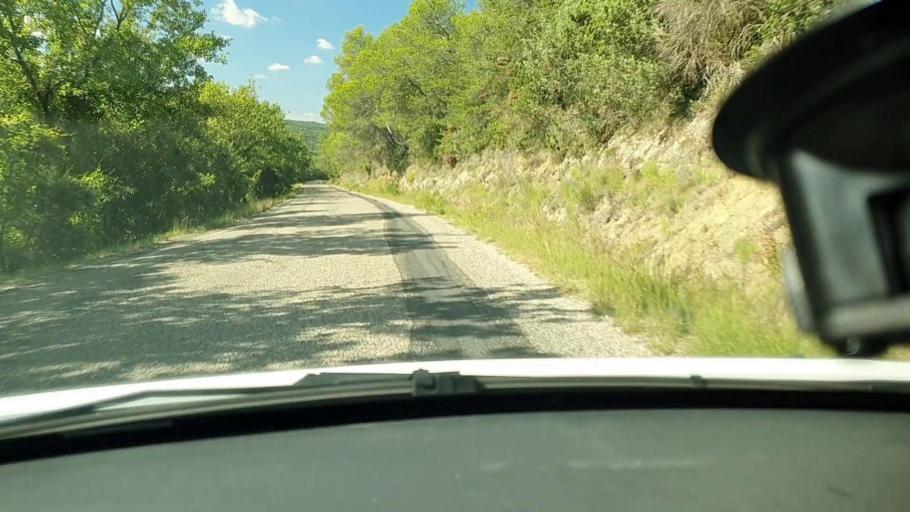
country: FR
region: Languedoc-Roussillon
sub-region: Departement du Gard
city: Goudargues
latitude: 44.1366
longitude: 4.4704
